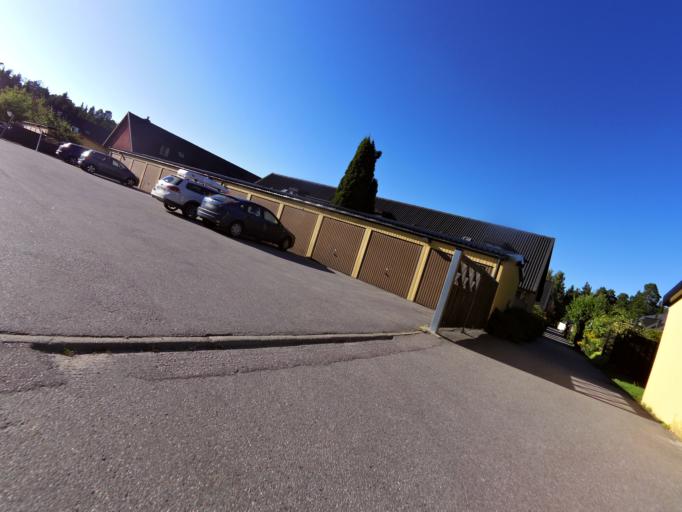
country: SE
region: Gaevleborg
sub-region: Gavle Kommun
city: Gavle
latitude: 60.6532
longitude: 17.1464
